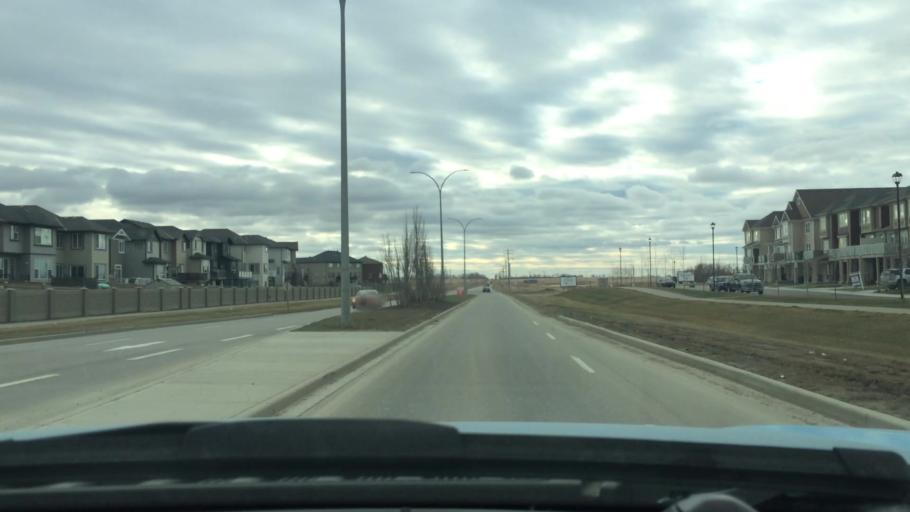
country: CA
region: Alberta
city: Airdrie
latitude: 51.2525
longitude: -114.0252
